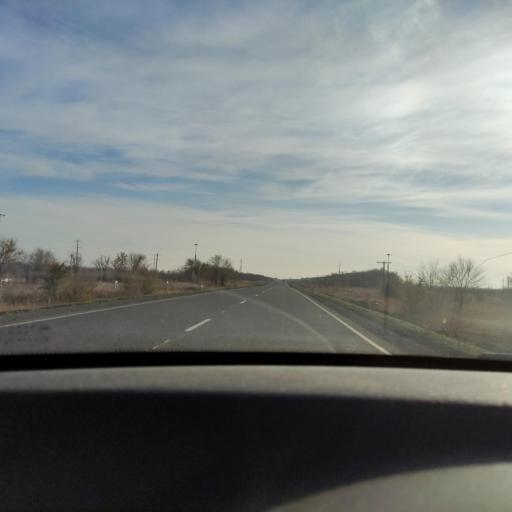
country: RU
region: Samara
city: Krasnoarmeyskoye
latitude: 52.8097
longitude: 50.0121
